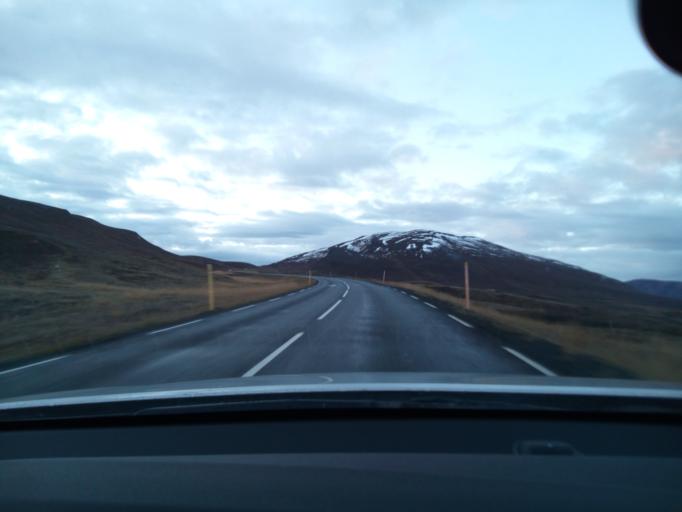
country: IS
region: Northeast
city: Akureyri
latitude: 65.7909
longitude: -17.9311
